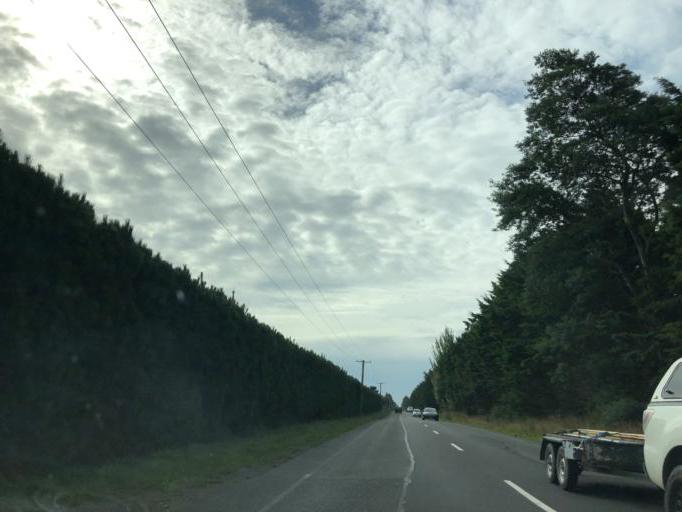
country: NZ
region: Canterbury
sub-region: Selwyn District
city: Rolleston
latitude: -43.6192
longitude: 172.4023
